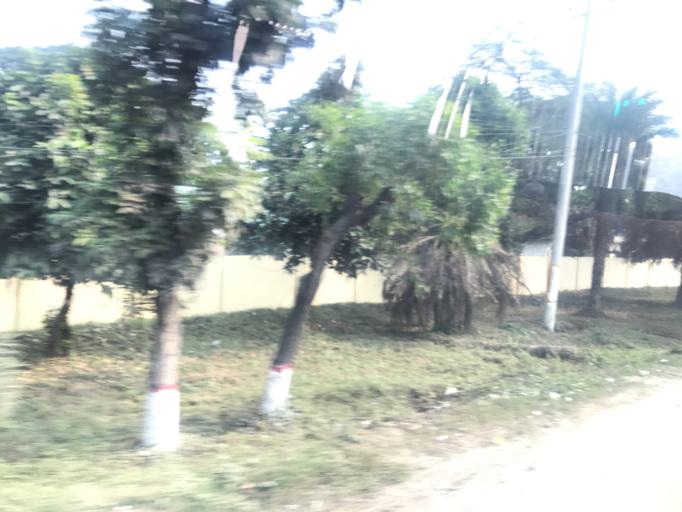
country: BD
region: Dhaka
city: Tungi
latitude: 23.8993
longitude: 90.2698
